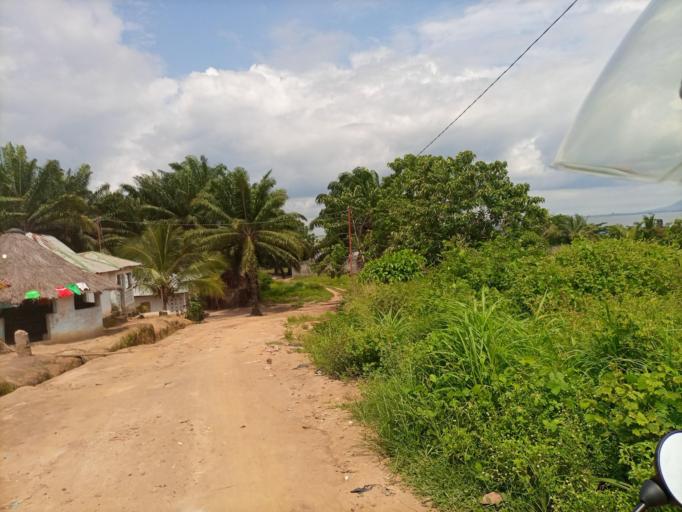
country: SL
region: Western Area
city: Freetown
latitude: 8.5260
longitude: -13.1436
